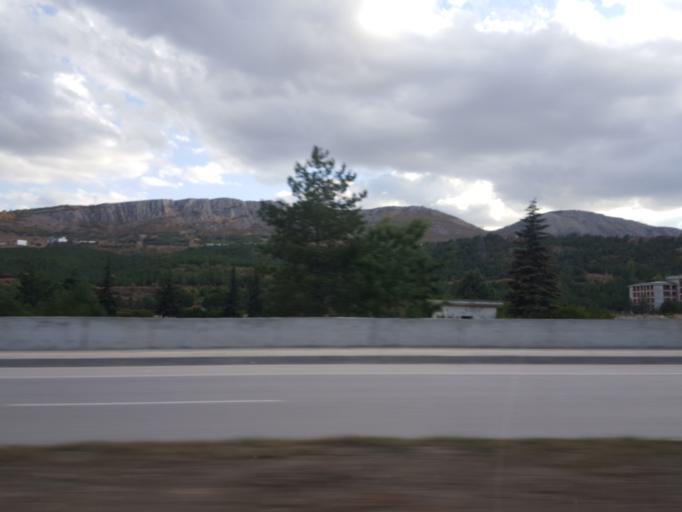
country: TR
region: Tokat
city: Tokat
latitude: 40.3354
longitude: 36.5067
